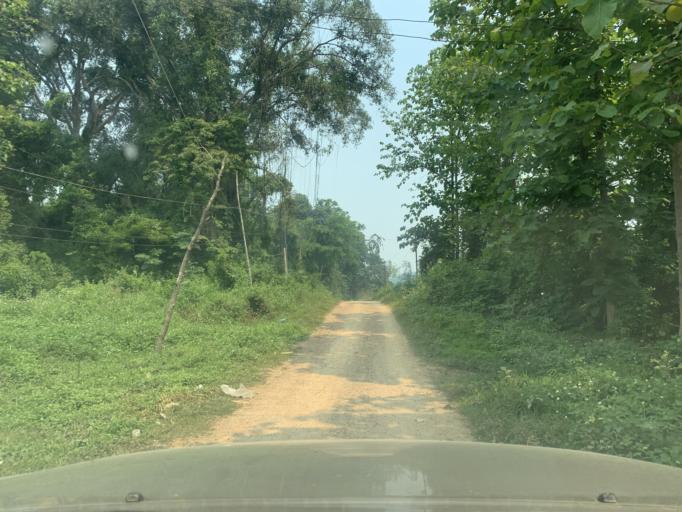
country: LA
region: Louangphabang
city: Xiang Ngeun
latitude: 19.8219
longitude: 102.2103
